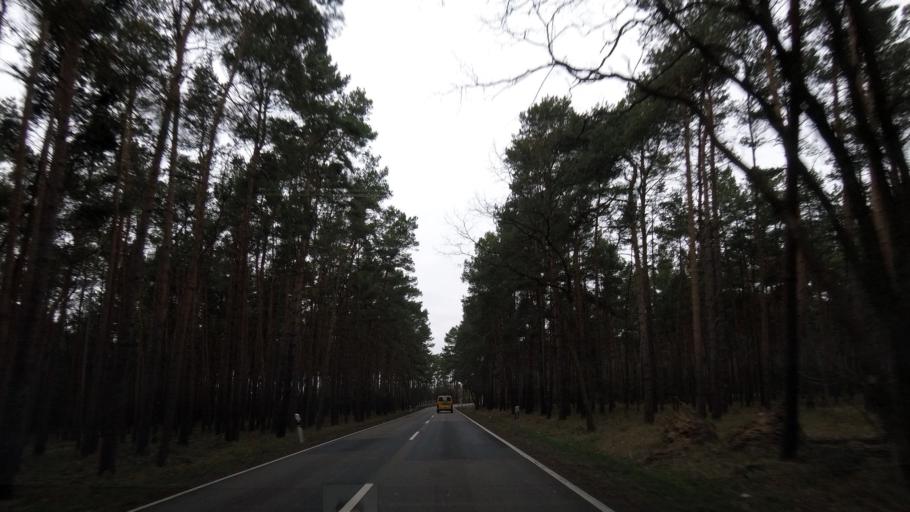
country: DE
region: Brandenburg
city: Linthe
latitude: 52.1397
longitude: 12.7912
